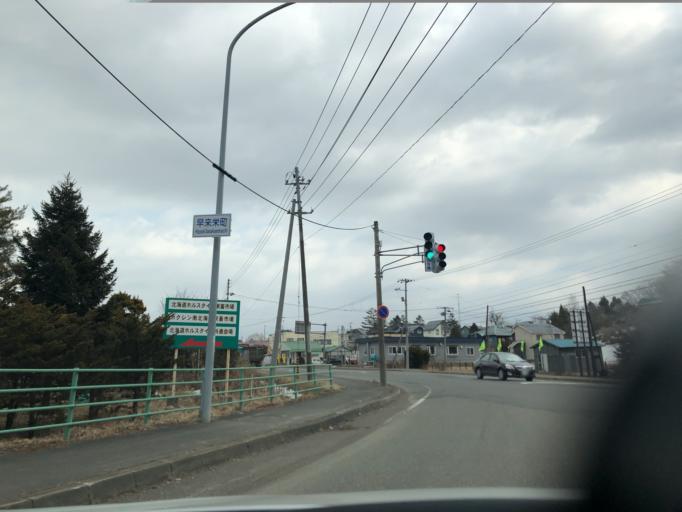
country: JP
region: Hokkaido
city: Chitose
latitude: 42.7621
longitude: 141.8123
